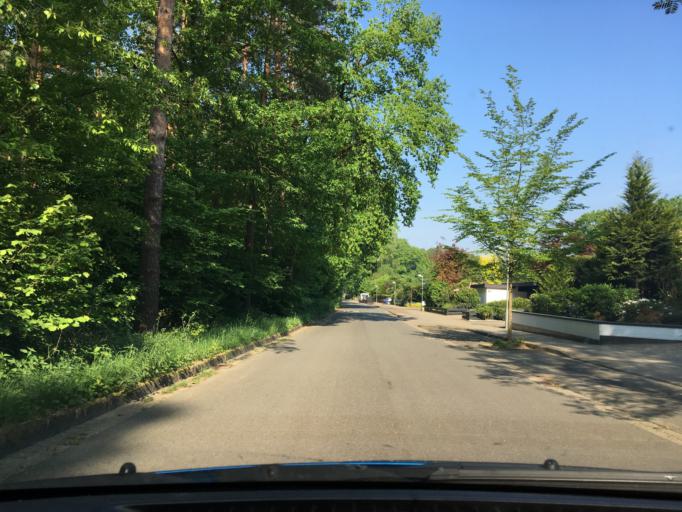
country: DE
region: Lower Saxony
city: Lueneburg
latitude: 53.2277
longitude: 10.4210
